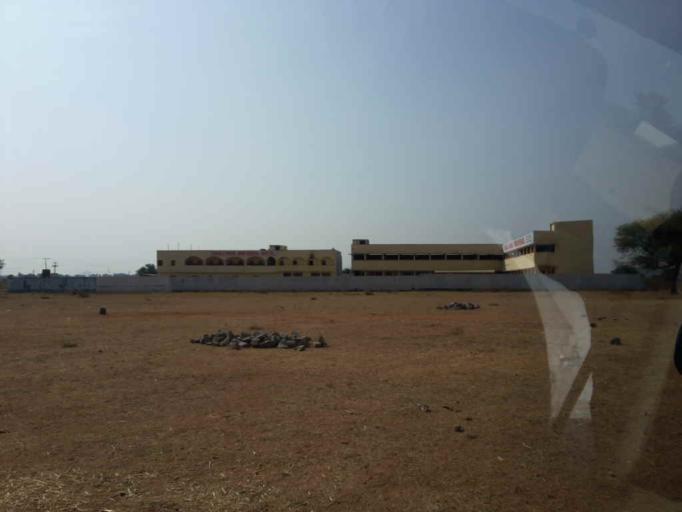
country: IN
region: Telangana
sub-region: Karimnagar
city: Sirsilla
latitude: 18.2972
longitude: 78.9520
